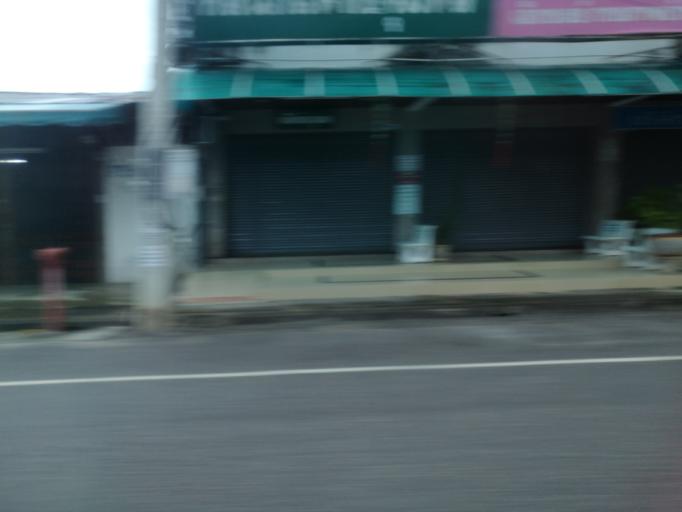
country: TH
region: Prachuap Khiri Khan
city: Prachuap Khiri Khan
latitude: 11.8052
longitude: 99.7957
